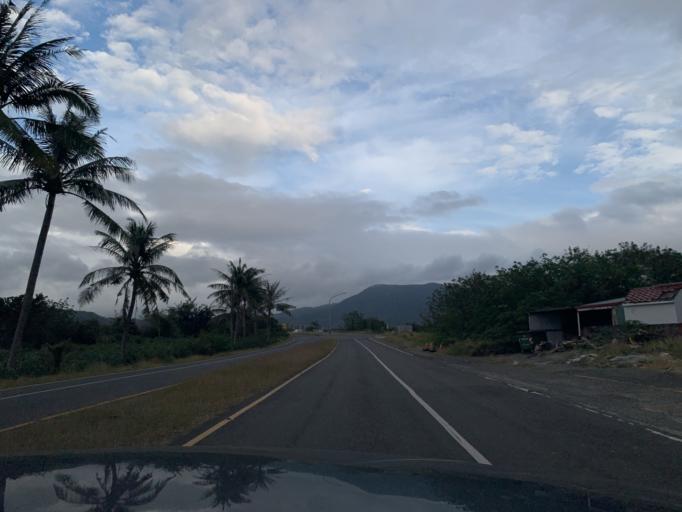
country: TW
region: Taiwan
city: Hengchun
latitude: 22.0522
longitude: 120.7176
